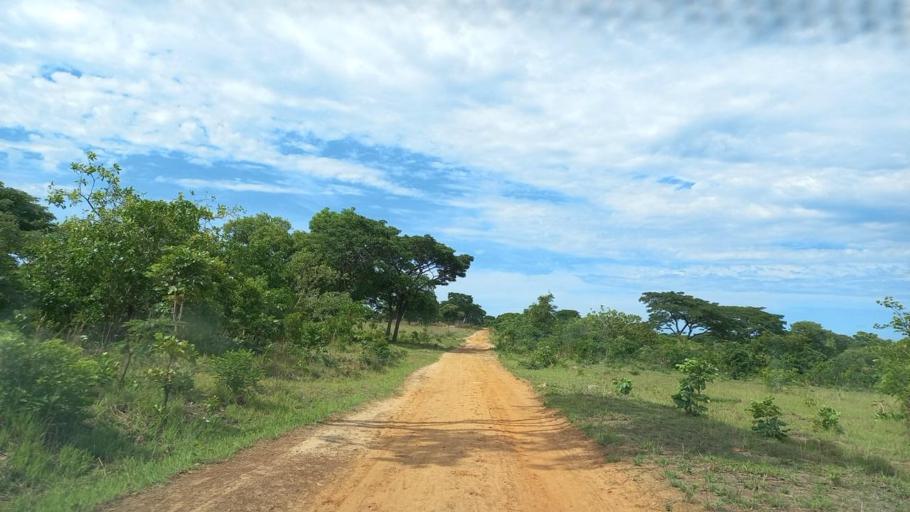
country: ZM
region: North-Western
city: Kabompo
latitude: -13.5116
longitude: 24.3930
